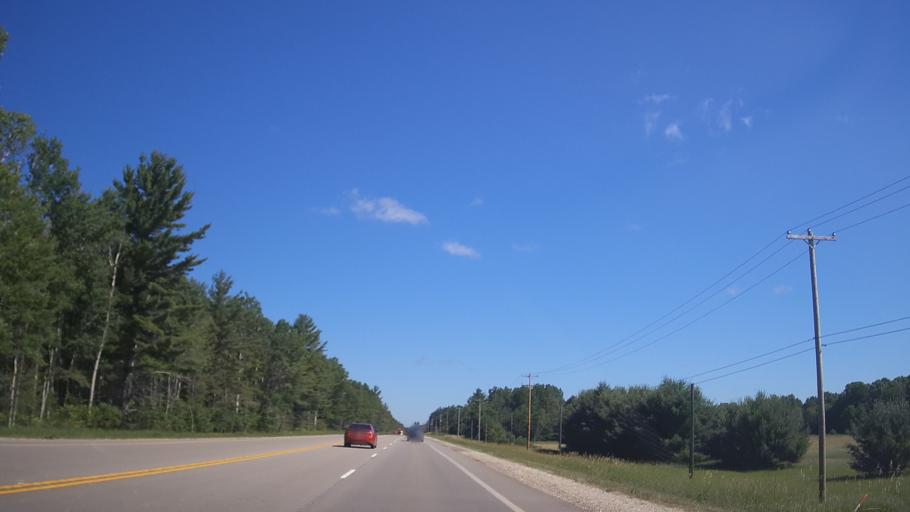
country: US
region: Michigan
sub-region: Cheboygan County
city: Indian River
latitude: 45.5118
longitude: -84.7814
